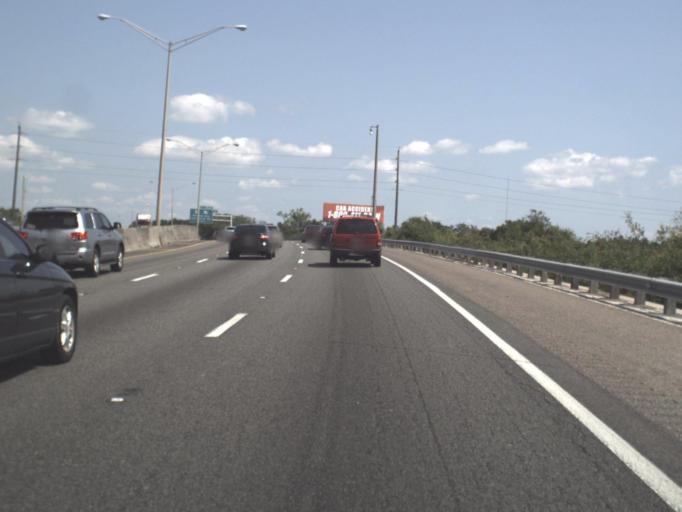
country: US
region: Florida
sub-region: Duval County
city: Jacksonville
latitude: 30.3719
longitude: -81.6690
